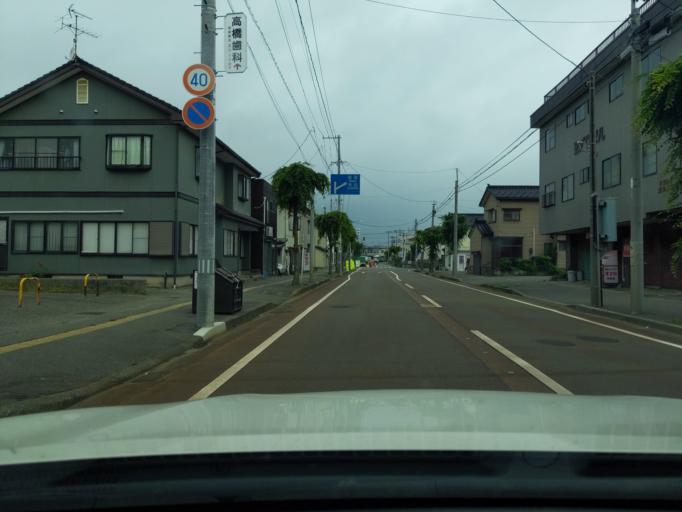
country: JP
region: Niigata
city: Kashiwazaki
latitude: 37.3722
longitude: 138.5577
